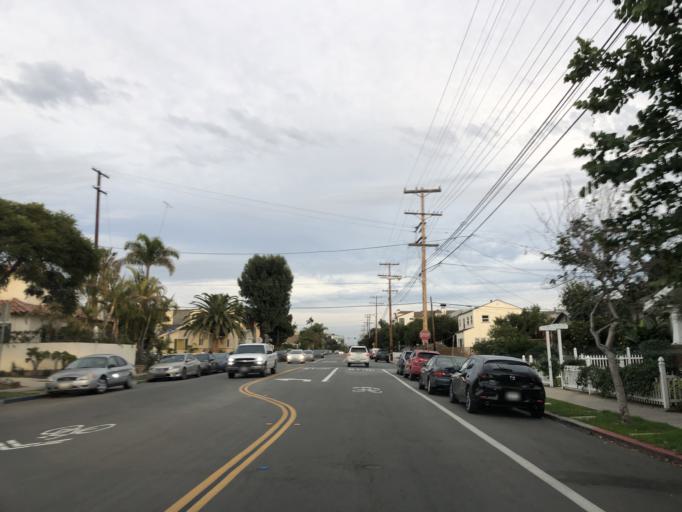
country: US
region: California
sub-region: San Diego County
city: San Diego
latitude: 32.7463
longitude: -117.1541
